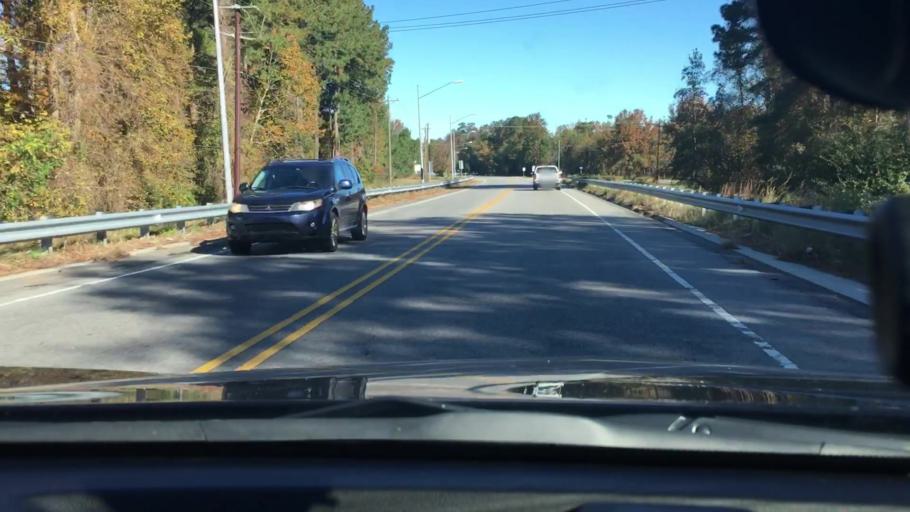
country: US
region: North Carolina
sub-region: Edgecombe County
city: Tarboro
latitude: 35.9124
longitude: -77.5622
